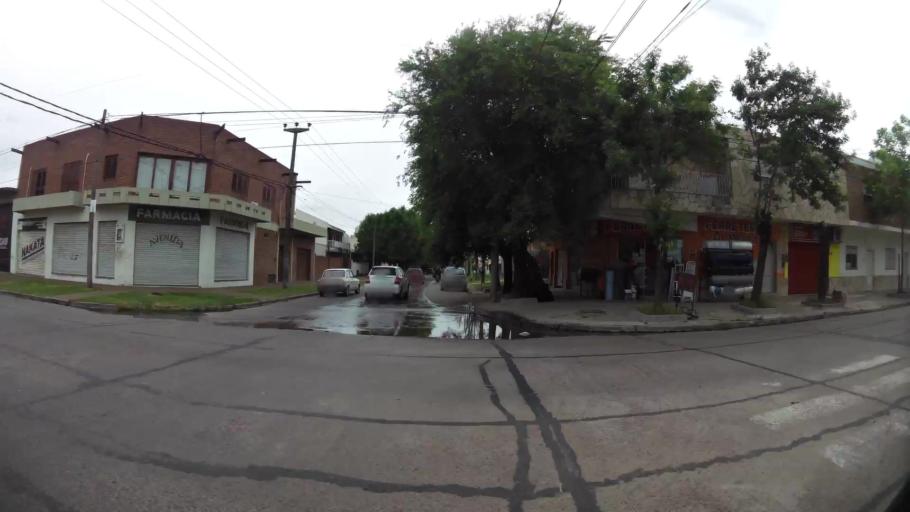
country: AR
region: Buenos Aires
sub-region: Partido de Campana
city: Campana
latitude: -34.1758
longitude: -58.9582
